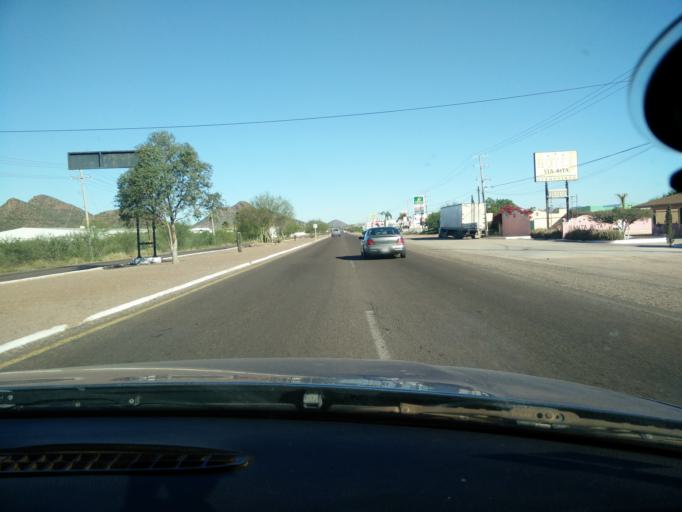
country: MX
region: Sonora
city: Heroica Guaymas
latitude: 27.9541
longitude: -110.9345
